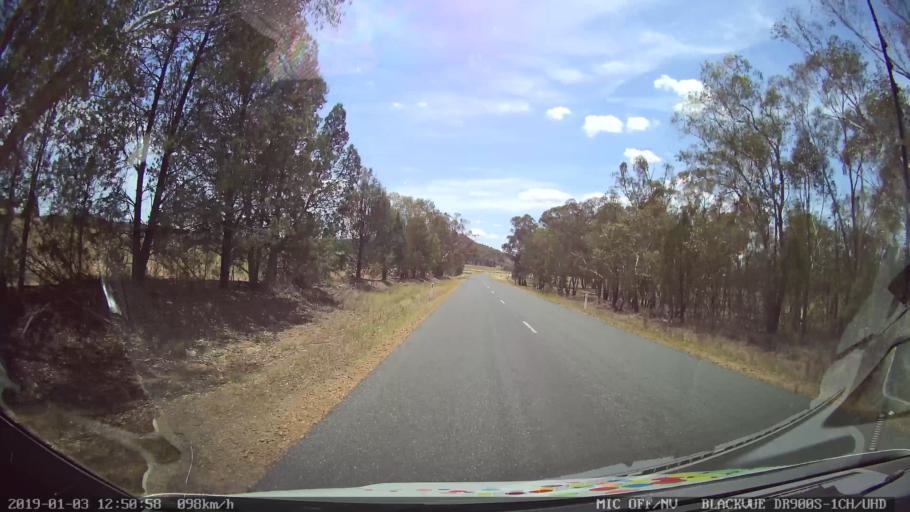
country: AU
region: New South Wales
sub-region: Weddin
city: Grenfell
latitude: -33.6850
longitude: 148.2754
